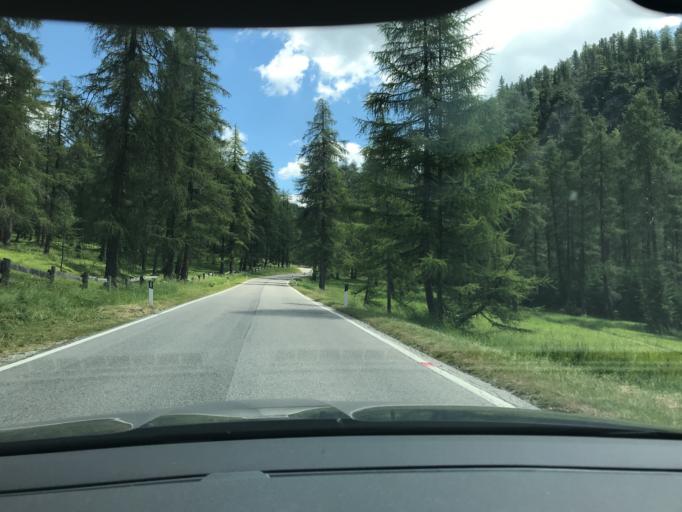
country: IT
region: Veneto
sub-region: Provincia di Belluno
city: Cortina d'Ampezzo
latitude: 46.5497
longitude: 12.1799
